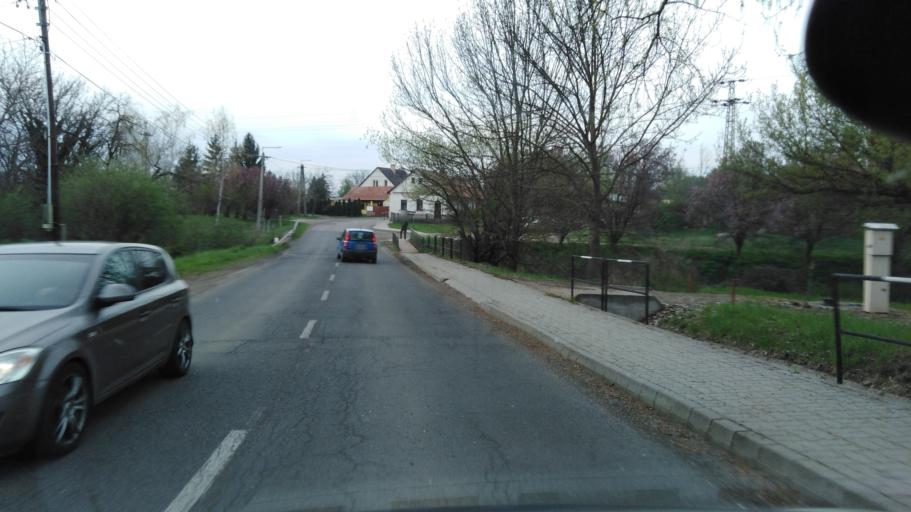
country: HU
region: Nograd
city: Batonyterenye
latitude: 47.9909
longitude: 19.8421
